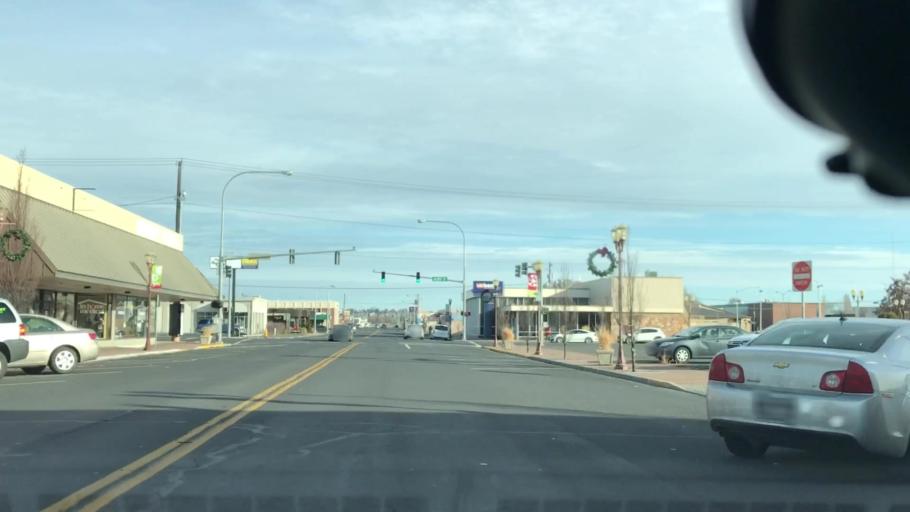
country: US
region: Washington
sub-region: Grant County
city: Moses Lake
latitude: 47.1304
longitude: -119.2776
